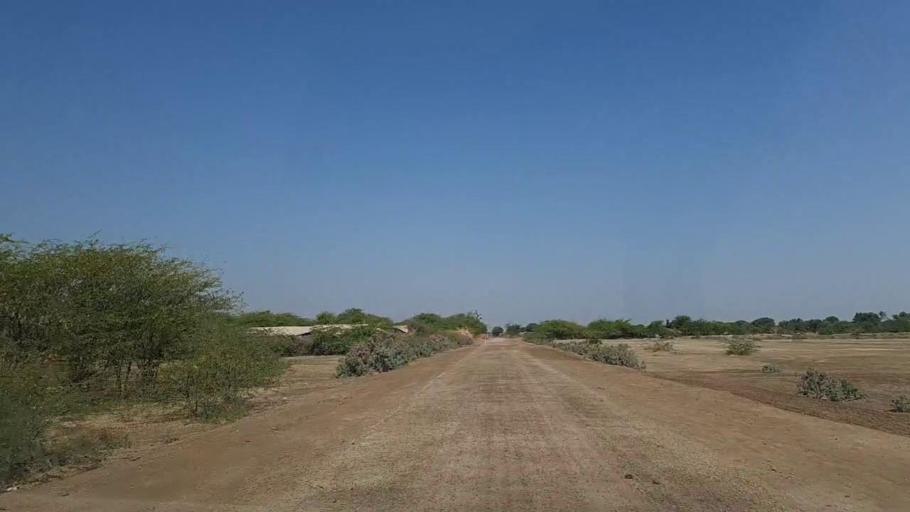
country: PK
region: Sindh
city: Samaro
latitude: 25.2461
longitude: 69.4484
